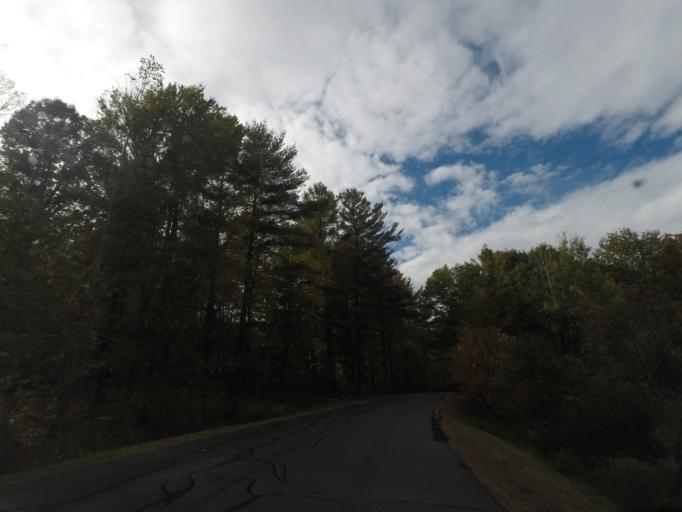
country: US
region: New York
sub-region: Rensselaer County
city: East Greenbush
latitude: 42.5796
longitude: -73.6447
